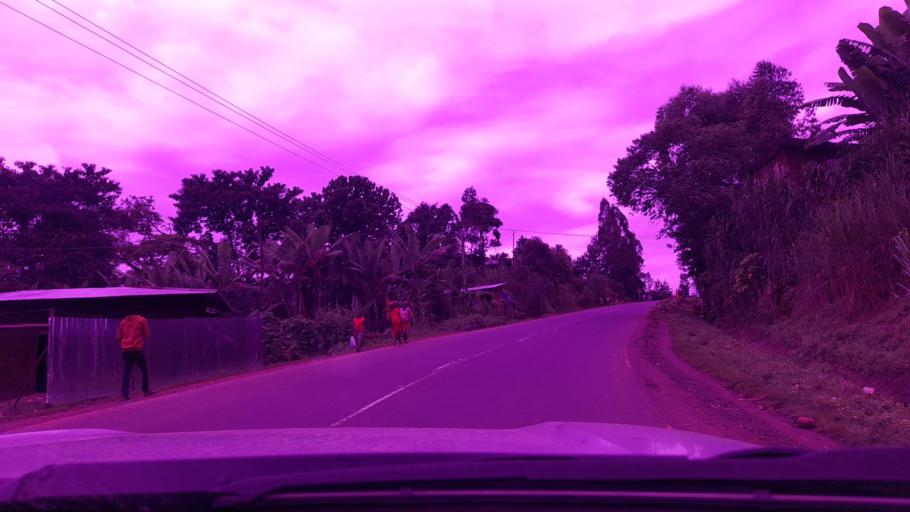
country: ET
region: Southern Nations, Nationalities, and People's Region
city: Mizan Teferi
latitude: 7.0076
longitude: 35.6108
